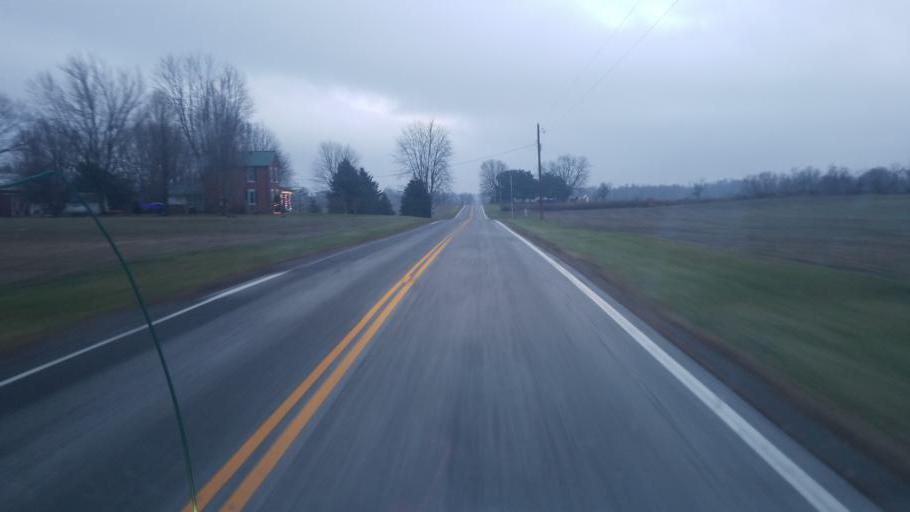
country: US
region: Ohio
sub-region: Wyandot County
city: Upper Sandusky
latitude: 40.8570
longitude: -83.1316
